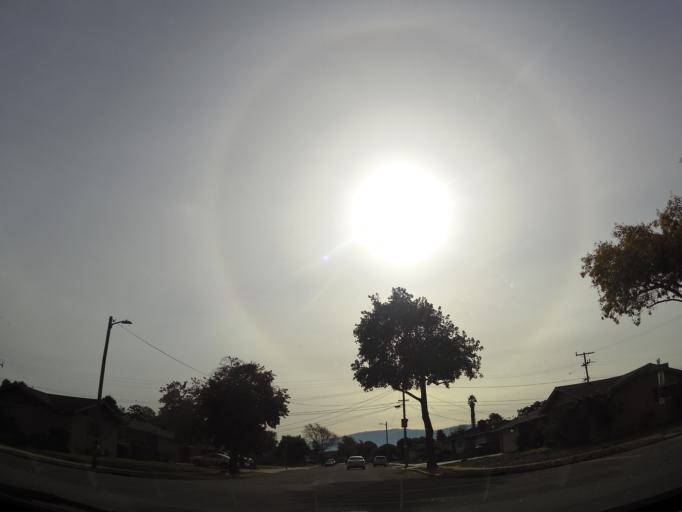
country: US
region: California
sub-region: Monterey County
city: Salinas
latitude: 36.6696
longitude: -121.6790
